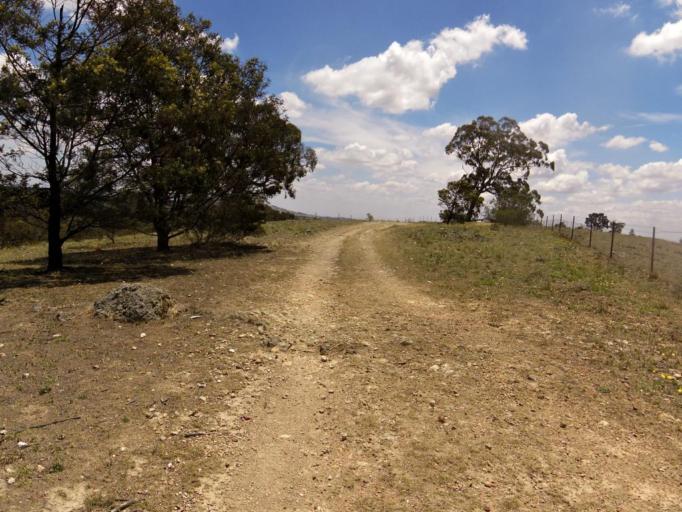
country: AU
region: Australian Capital Territory
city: Kaleen
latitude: -35.1446
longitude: 149.1467
